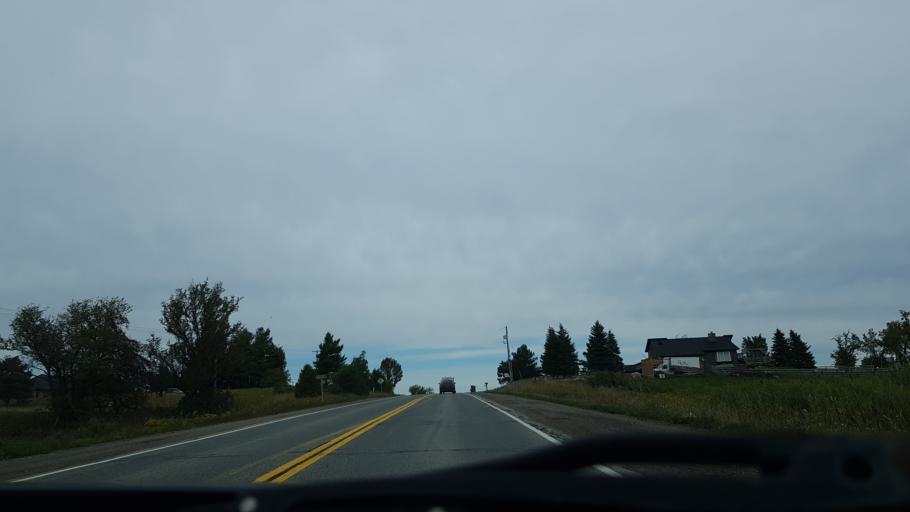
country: CA
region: Ontario
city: Orangeville
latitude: 43.8900
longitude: -79.9626
